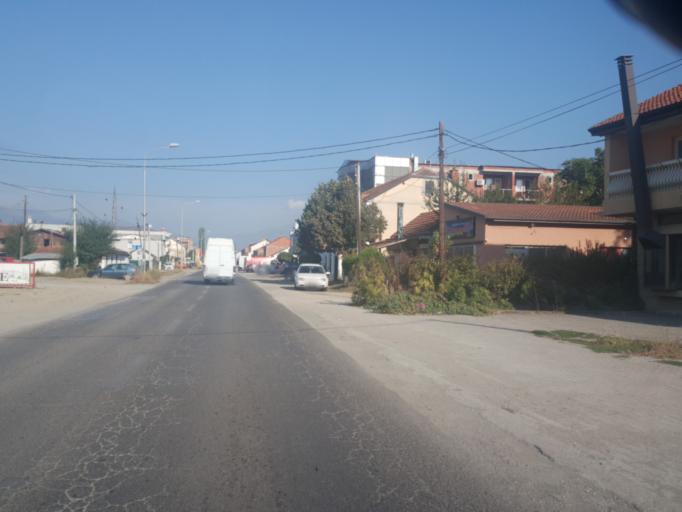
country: XK
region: Gjakova
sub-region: Komuna e Gjakoves
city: Gjakove
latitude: 42.3984
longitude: 20.4182
